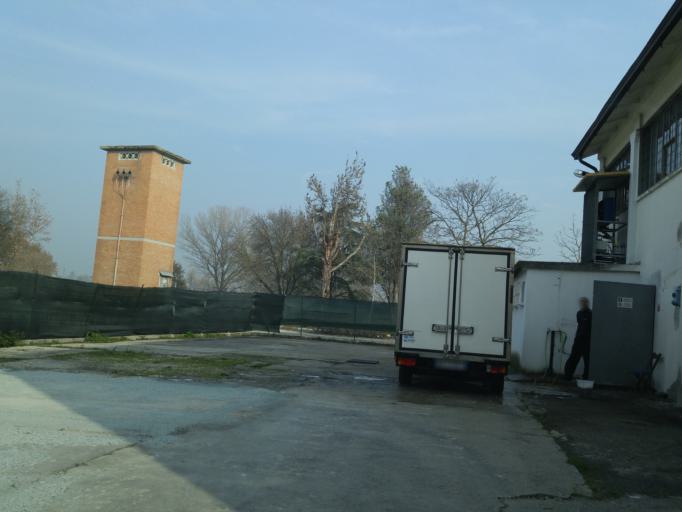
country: IT
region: Emilia-Romagna
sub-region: Provincia di Rimini
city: Montalbano
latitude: 43.9503
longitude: 12.7221
